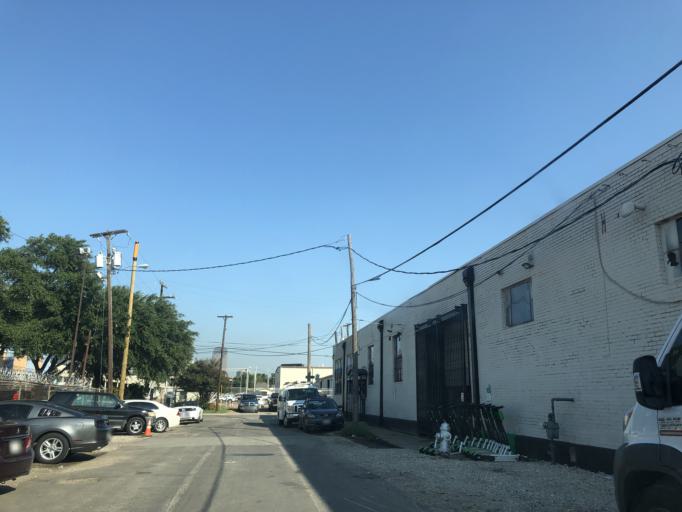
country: US
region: Texas
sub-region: Dallas County
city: Dallas
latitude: 32.7718
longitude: -96.7755
